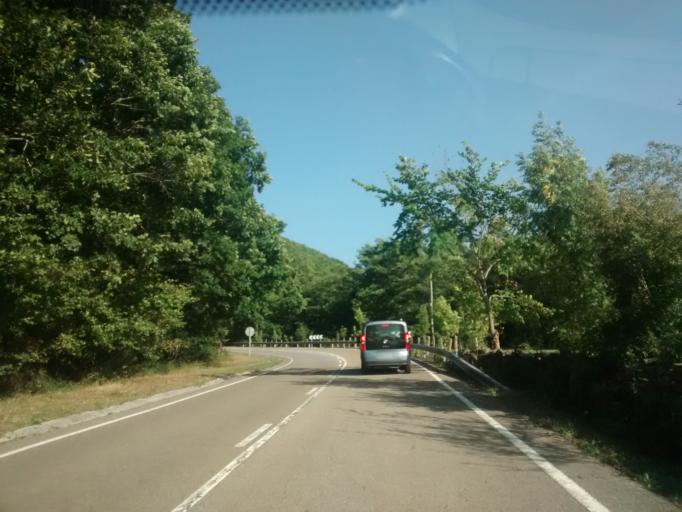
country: ES
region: Cantabria
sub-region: Provincia de Cantabria
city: Ruente
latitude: 43.1516
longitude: -4.2212
